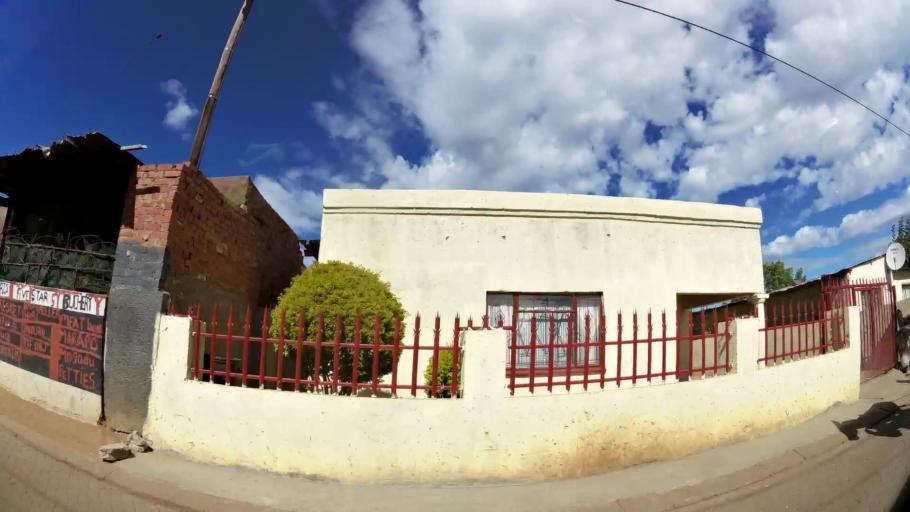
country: ZA
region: Limpopo
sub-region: Waterberg District Municipality
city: Bela-Bela
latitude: -24.8855
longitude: 28.3267
